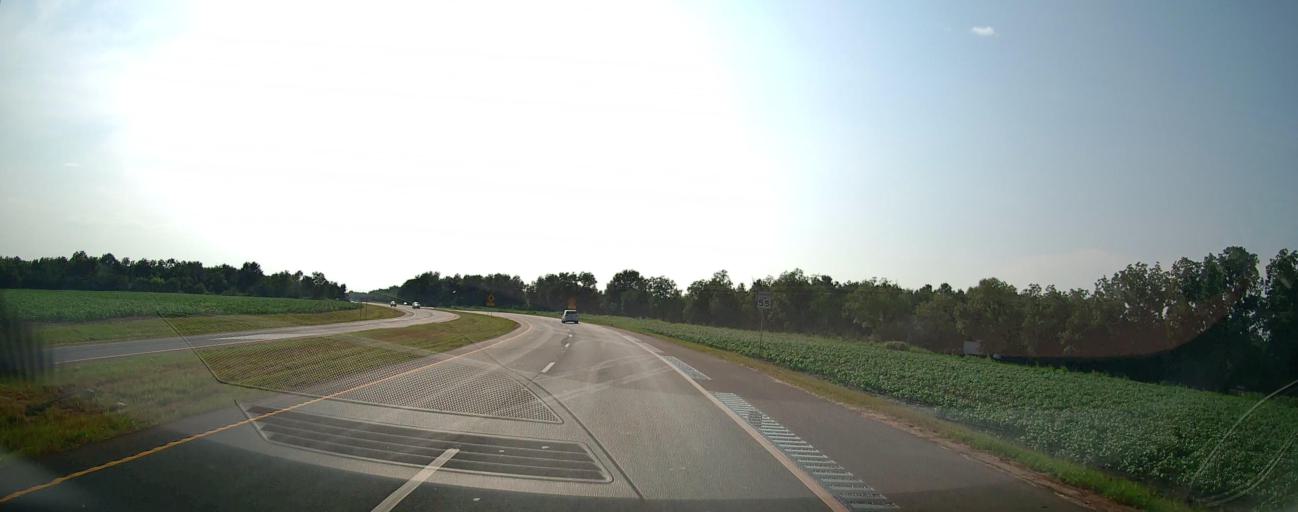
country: US
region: Georgia
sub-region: Peach County
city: Fort Valley
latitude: 32.5773
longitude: -83.8695
